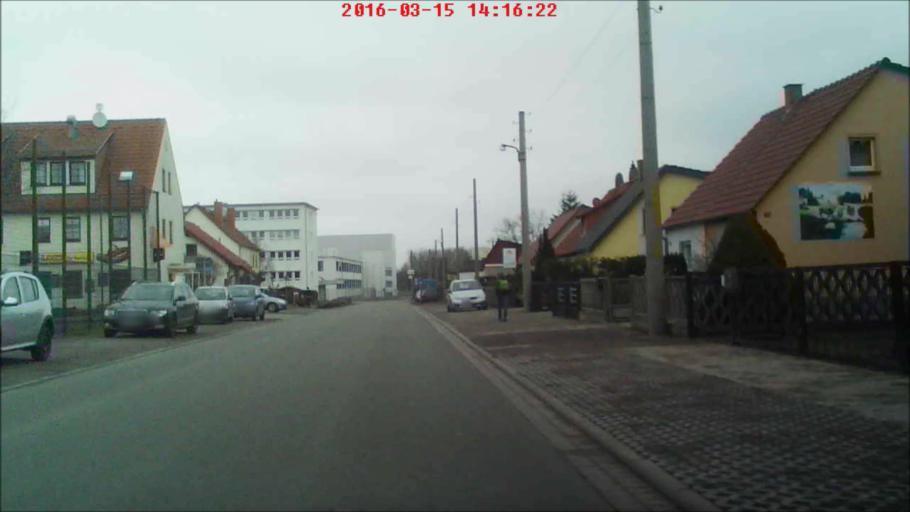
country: DE
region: Thuringia
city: Arnstadt
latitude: 50.8431
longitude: 10.9614
